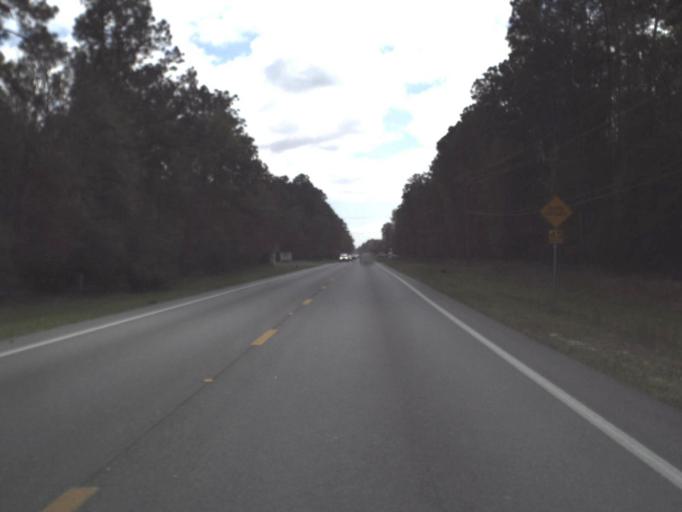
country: US
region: Florida
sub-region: Wakulla County
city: Crawfordville
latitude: 30.2482
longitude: -84.3624
